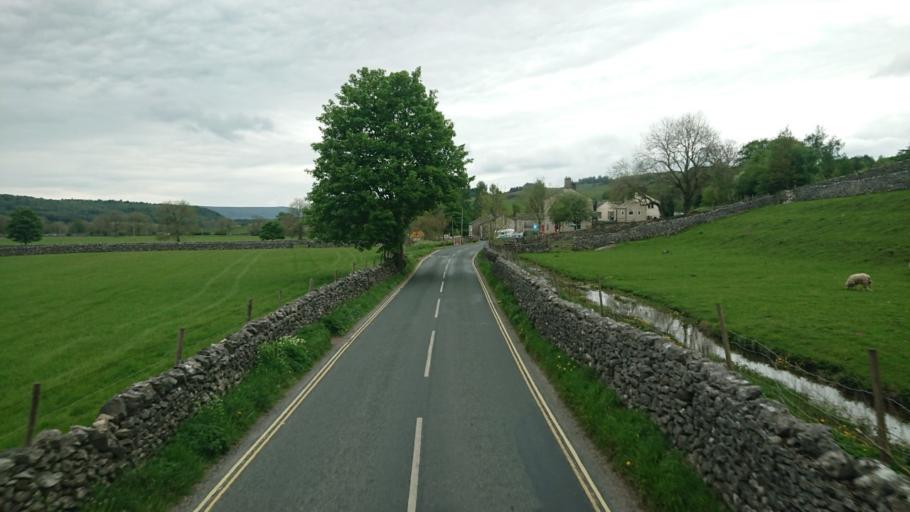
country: GB
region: England
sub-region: North Yorkshire
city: Embsay
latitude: 54.1078
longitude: -2.0397
